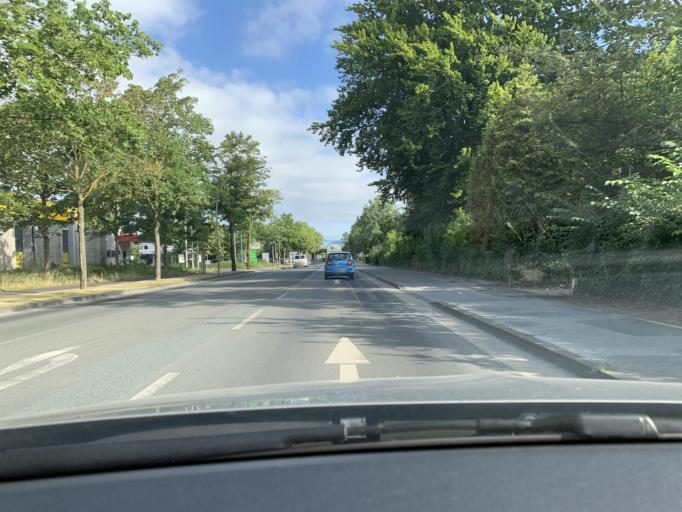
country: DE
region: North Rhine-Westphalia
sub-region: Regierungsbezirk Detmold
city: Rheda-Wiedenbruck
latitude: 51.8436
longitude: 8.2970
